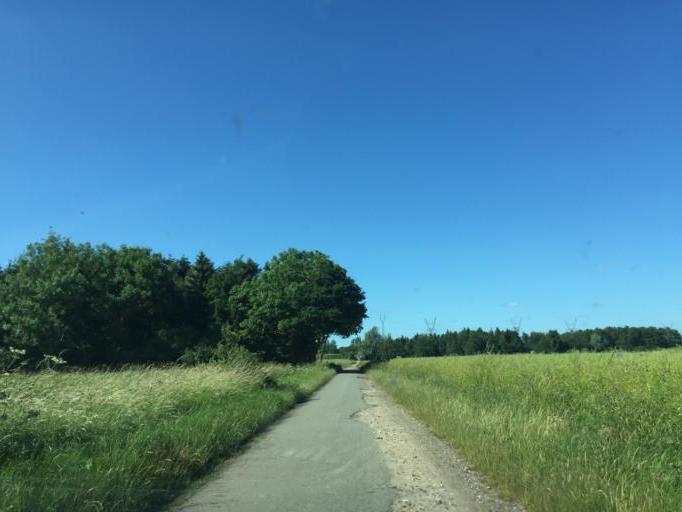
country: DK
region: South Denmark
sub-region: Odense Kommune
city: Neder Holluf
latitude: 55.3488
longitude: 10.4693
